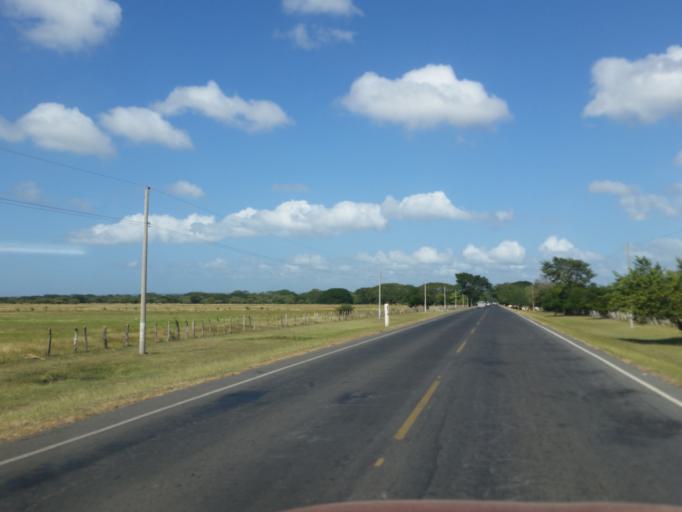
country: NI
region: Granada
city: Nandaime
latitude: 11.7045
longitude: -86.0044
